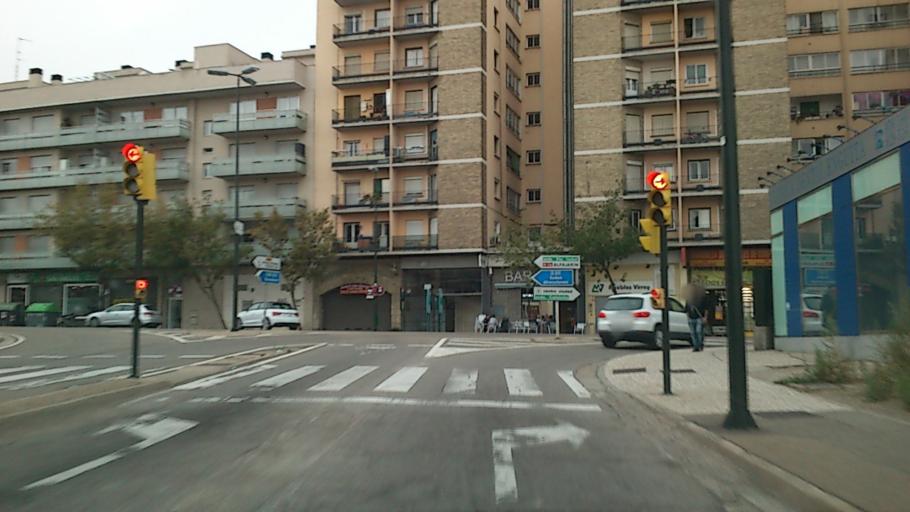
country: ES
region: Aragon
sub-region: Provincia de Zaragoza
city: Zaragoza
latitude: 41.6700
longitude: -0.8389
